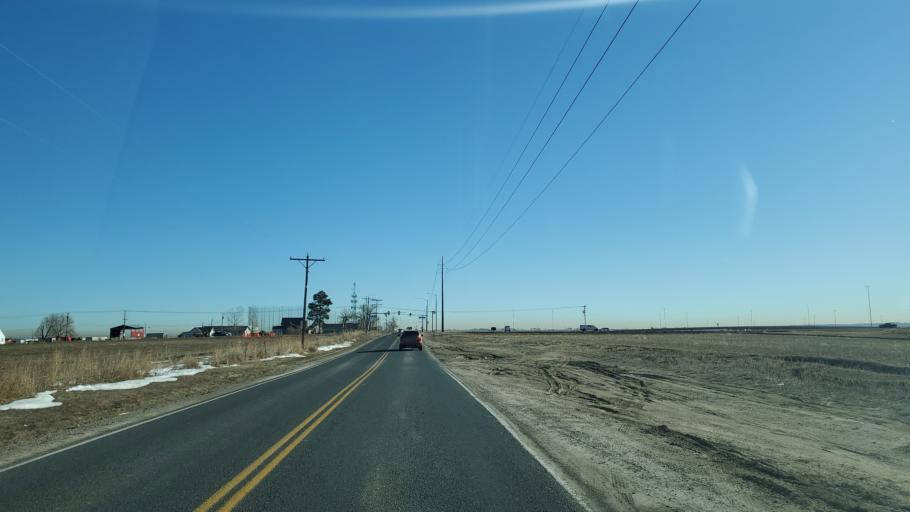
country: US
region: Colorado
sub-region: Boulder County
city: Erie
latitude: 39.9869
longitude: -105.0002
